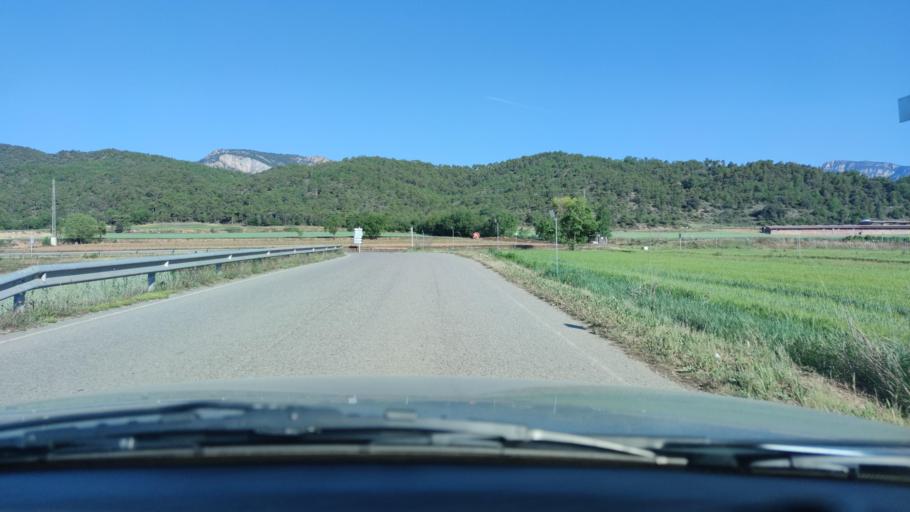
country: ES
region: Catalonia
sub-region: Provincia de Lleida
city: Oliana
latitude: 42.0351
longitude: 1.2885
